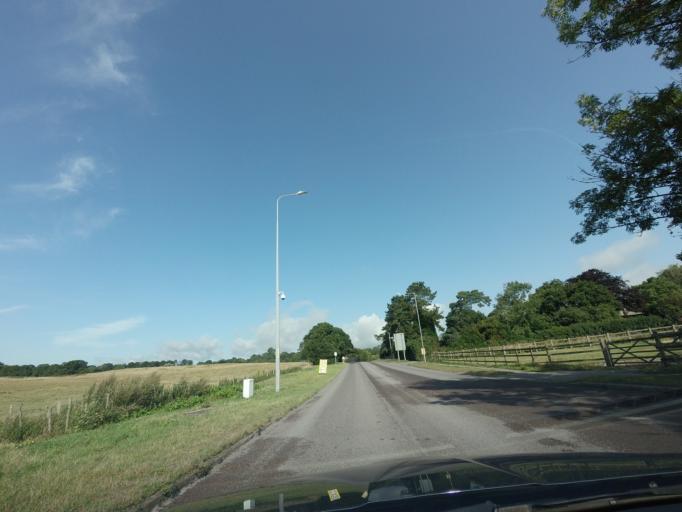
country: GB
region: England
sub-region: Kent
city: Harrietsham
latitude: 51.2627
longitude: 0.6085
